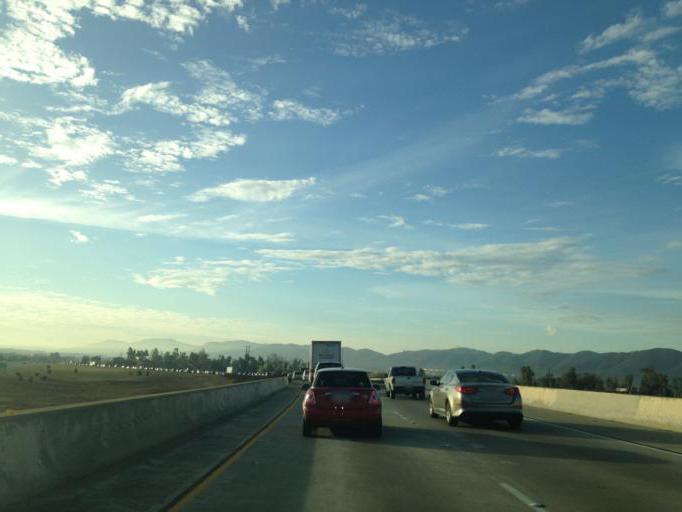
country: US
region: California
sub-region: Riverside County
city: Murrieta Hot Springs
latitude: 33.5488
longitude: -117.1816
